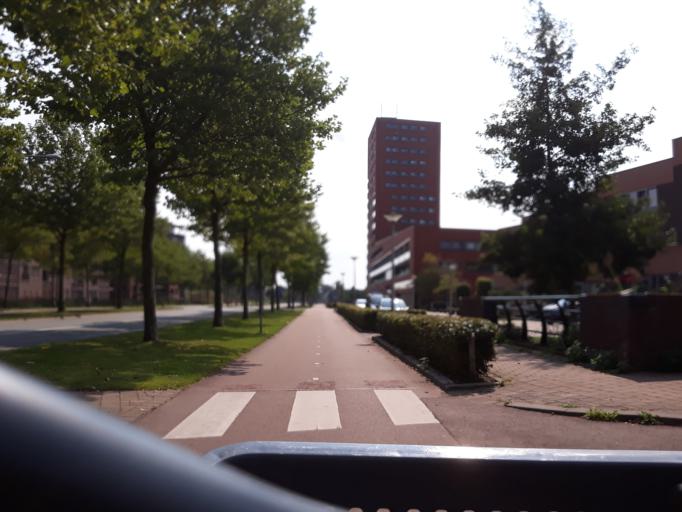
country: NL
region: South Holland
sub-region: Gemeente Hendrik-Ido-Ambacht
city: Hendrik-Ido-Ambacht
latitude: 51.8370
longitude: 4.6460
